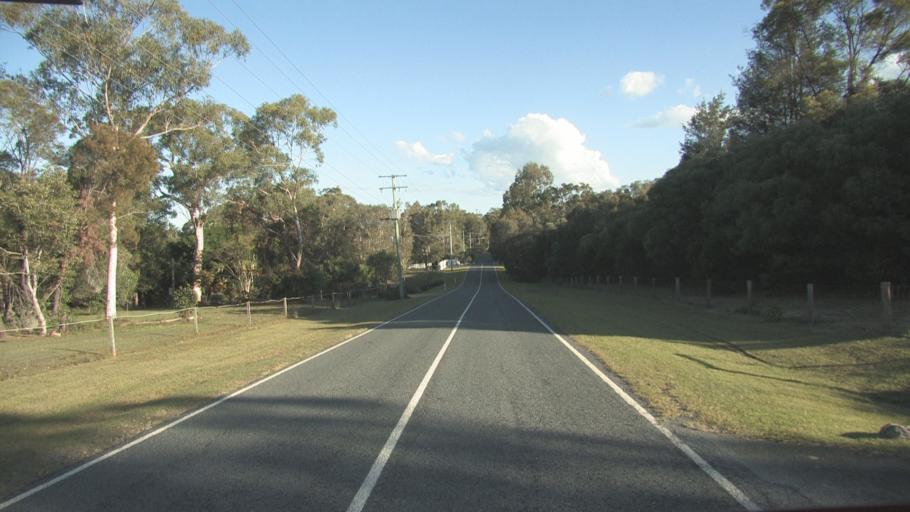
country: AU
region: Queensland
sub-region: Redland
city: Redland Bay
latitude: -27.6618
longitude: 153.2771
